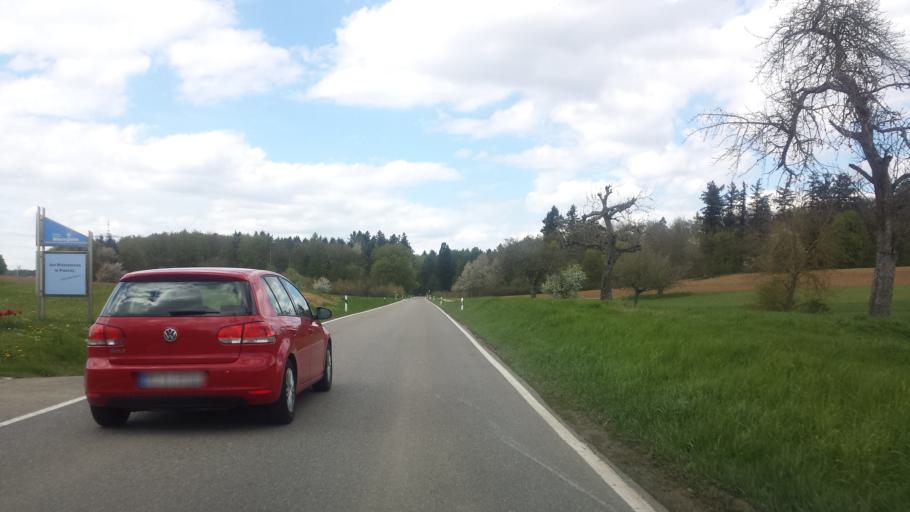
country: DE
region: Baden-Wuerttemberg
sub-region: Karlsruhe Region
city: Wiernsheim
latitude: 48.9118
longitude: 8.8471
